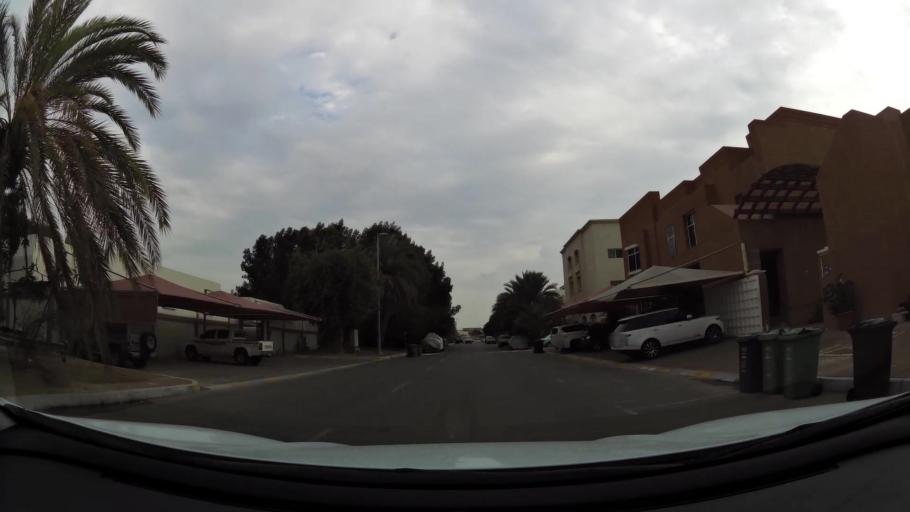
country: AE
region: Abu Dhabi
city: Abu Dhabi
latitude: 24.4395
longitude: 54.3931
